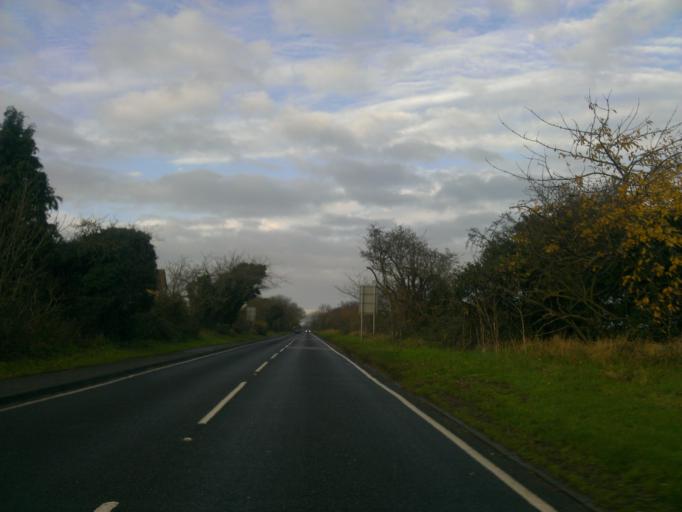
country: GB
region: England
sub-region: Essex
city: Saint Osyth
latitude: 51.8026
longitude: 1.0896
